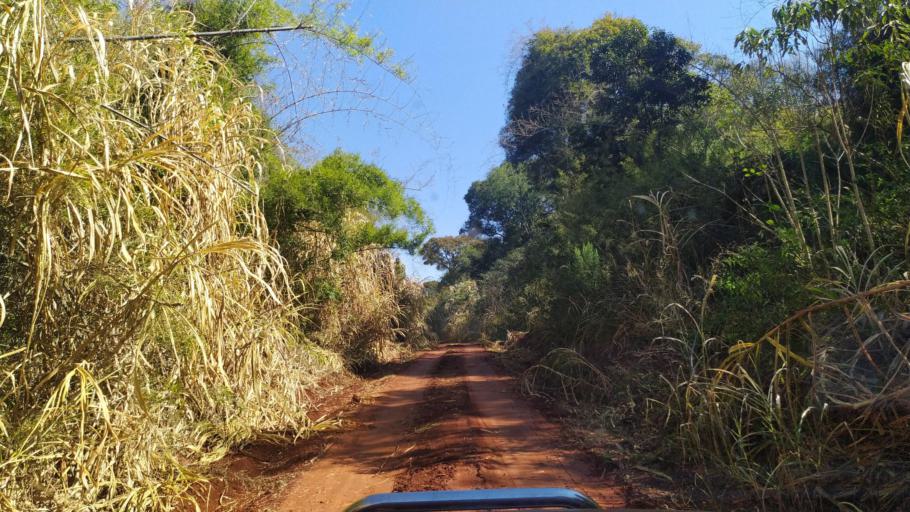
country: AR
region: Misiones
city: El Alcazar
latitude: -26.7519
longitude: -54.6048
